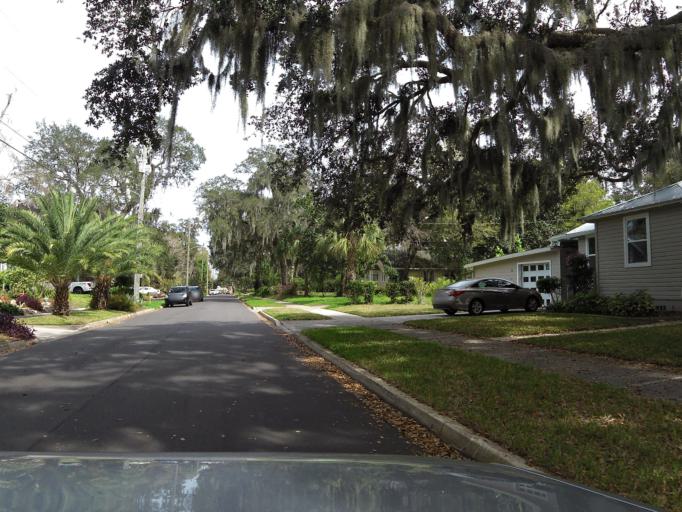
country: US
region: Florida
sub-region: Saint Johns County
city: Saint Augustine
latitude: 29.9158
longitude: -81.3203
